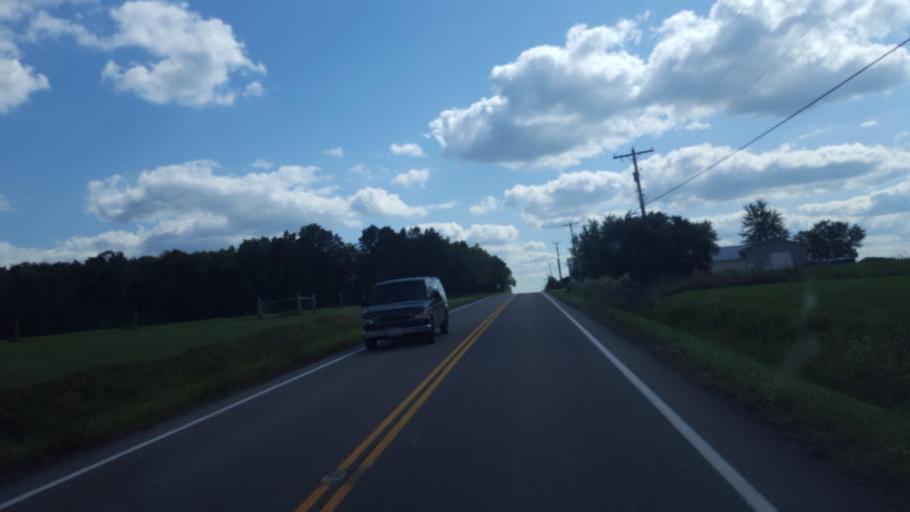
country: US
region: Ohio
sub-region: Wayne County
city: West Salem
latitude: 40.9592
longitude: -82.2149
